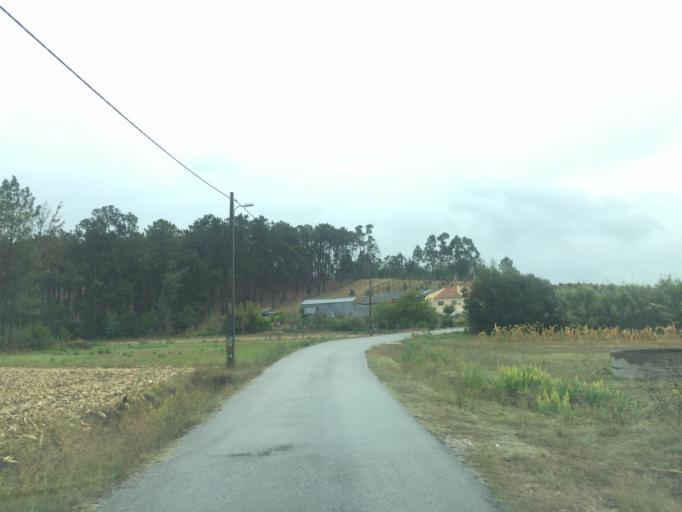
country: PT
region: Coimbra
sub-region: Figueira da Foz
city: Lavos
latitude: 40.0667
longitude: -8.7817
